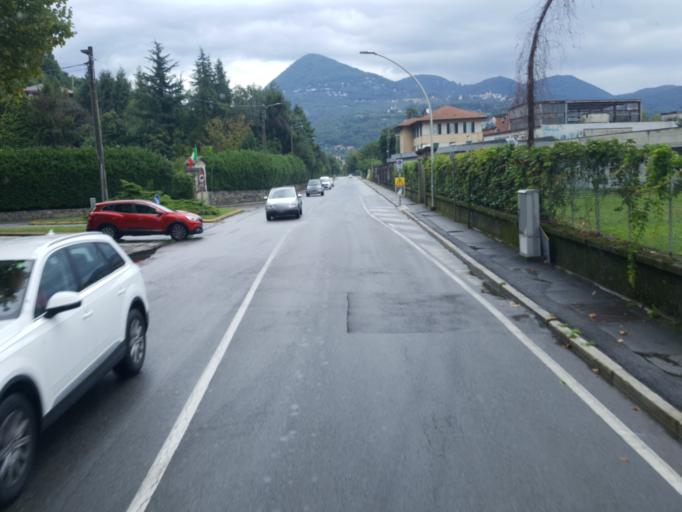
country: IT
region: Piedmont
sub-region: Provincia Verbano-Cusio-Ossola
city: Verbania
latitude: 45.9331
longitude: 8.5541
